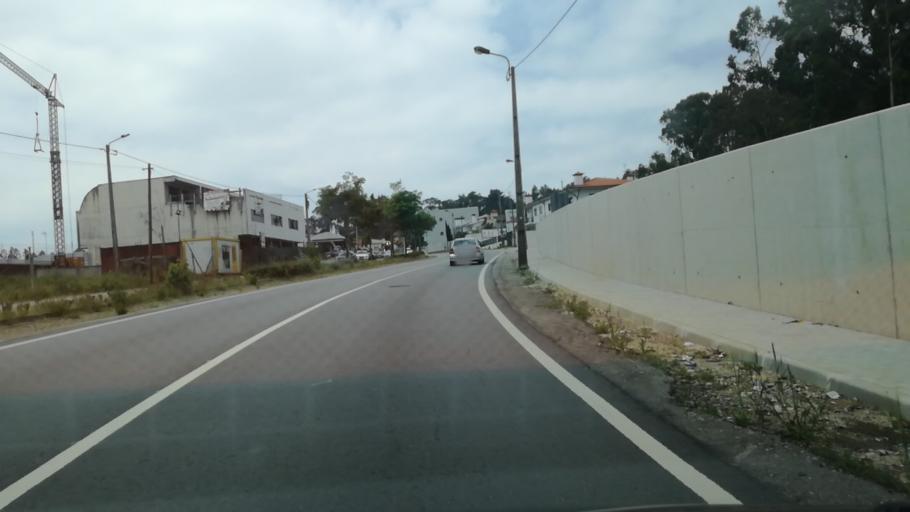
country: PT
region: Porto
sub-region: Trofa
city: Sao Romao do Coronado
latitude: 41.3067
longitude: -8.5831
